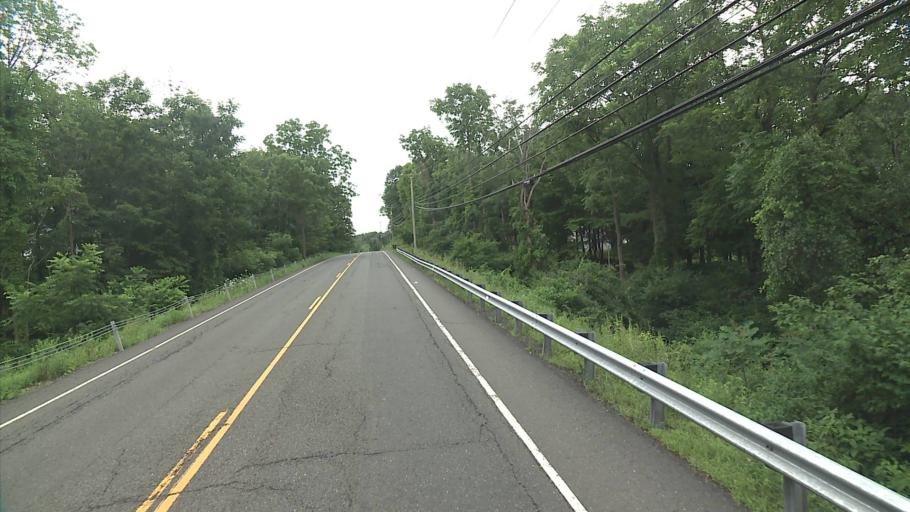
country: US
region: Connecticut
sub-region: Litchfield County
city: New Milford
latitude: 41.5512
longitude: -73.3812
